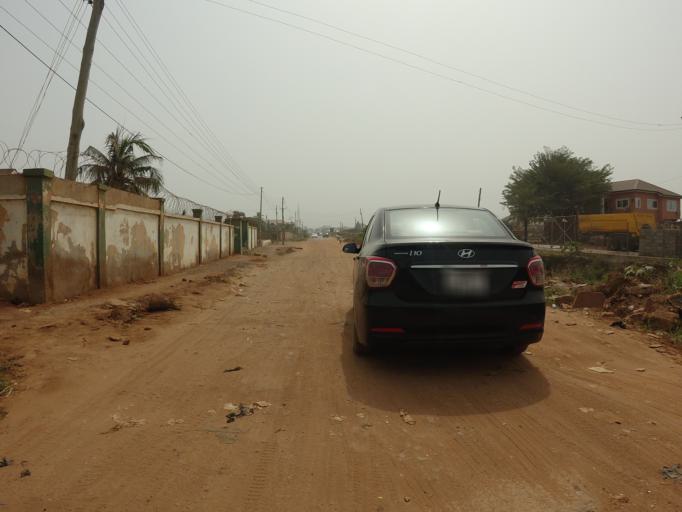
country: GH
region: Greater Accra
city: Nungua
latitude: 5.6464
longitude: -0.1005
